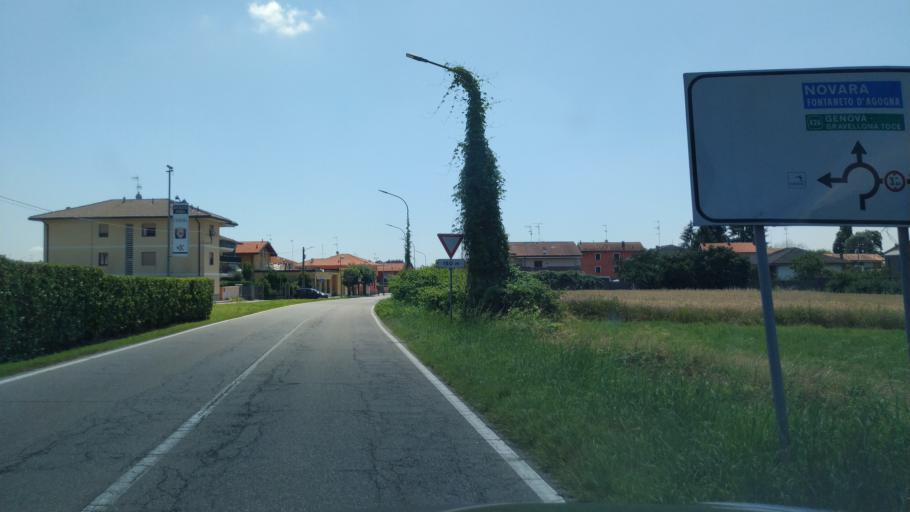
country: IT
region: Piedmont
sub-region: Provincia di Novara
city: Cureggio
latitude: 45.6792
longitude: 8.4618
